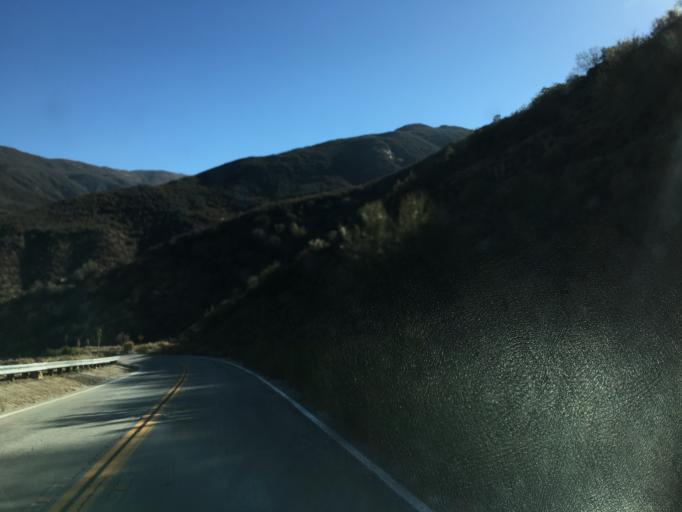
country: US
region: California
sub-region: Los Angeles County
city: Castaic
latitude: 34.5743
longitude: -118.5568
